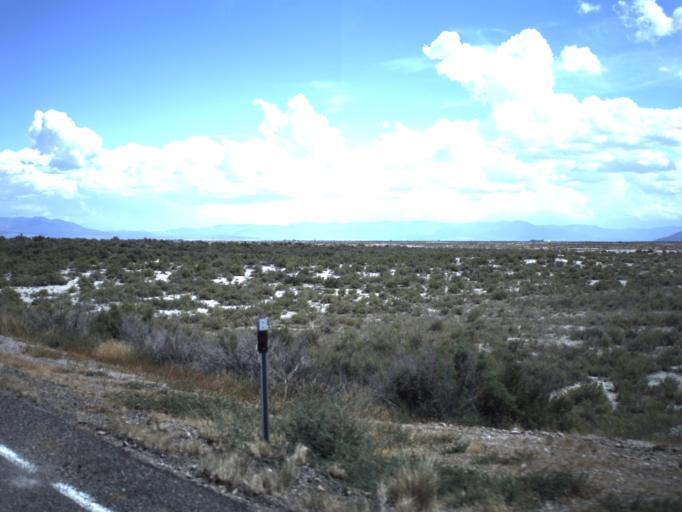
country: US
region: Utah
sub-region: Millard County
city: Delta
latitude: 39.3076
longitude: -112.7892
